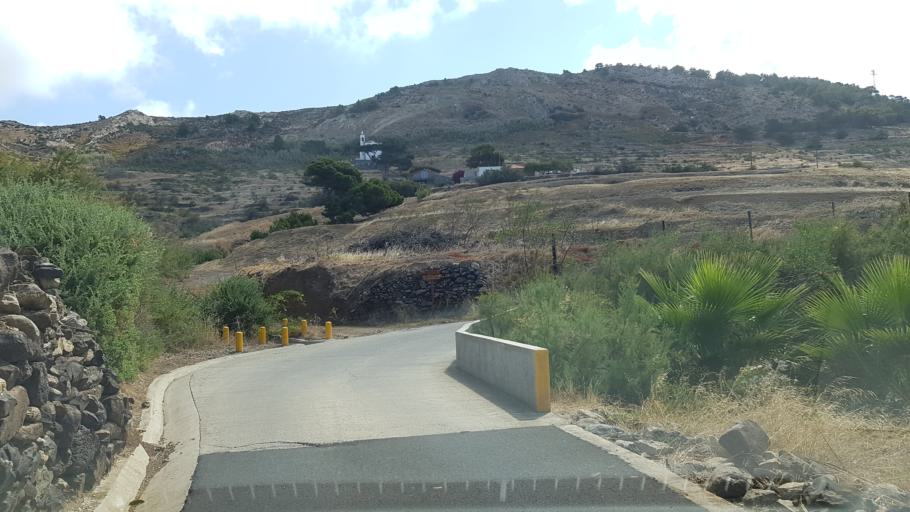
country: PT
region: Madeira
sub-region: Porto Santo
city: Vila de Porto Santo
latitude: 33.0721
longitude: -16.3274
